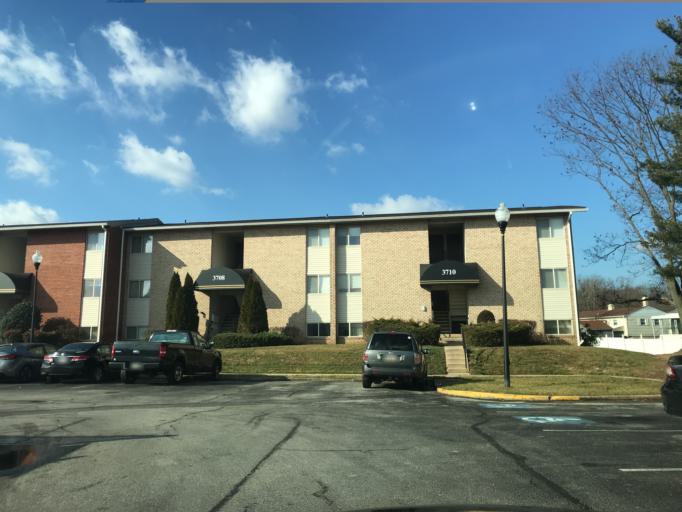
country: US
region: Maryland
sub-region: Baltimore County
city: Bowleys Quarters
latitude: 39.3314
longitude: -76.3935
